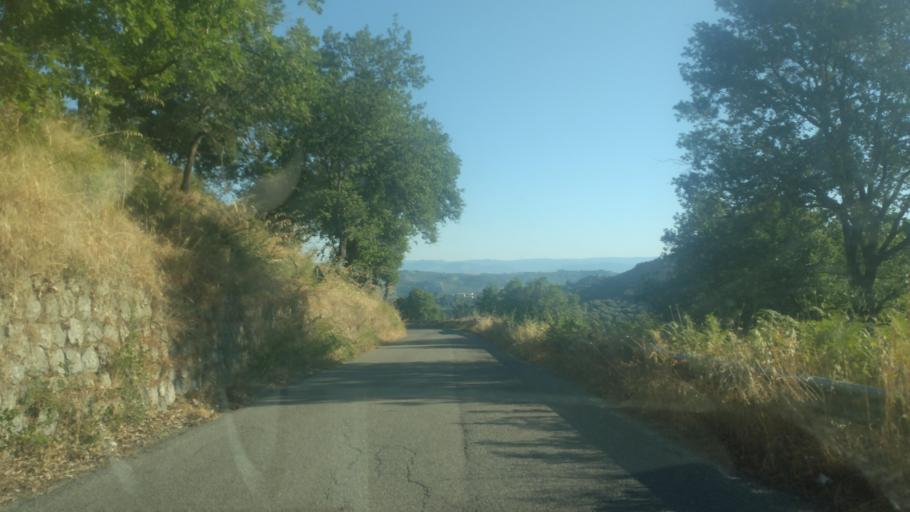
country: IT
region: Calabria
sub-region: Provincia di Catanzaro
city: Squillace
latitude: 38.7678
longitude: 16.5137
